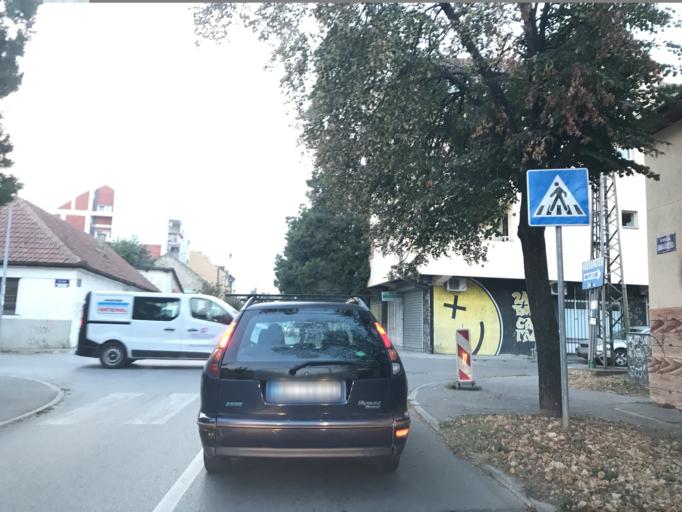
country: RS
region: Autonomna Pokrajina Vojvodina
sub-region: Juznobacki Okrug
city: Novi Sad
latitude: 45.2664
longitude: 19.8408
